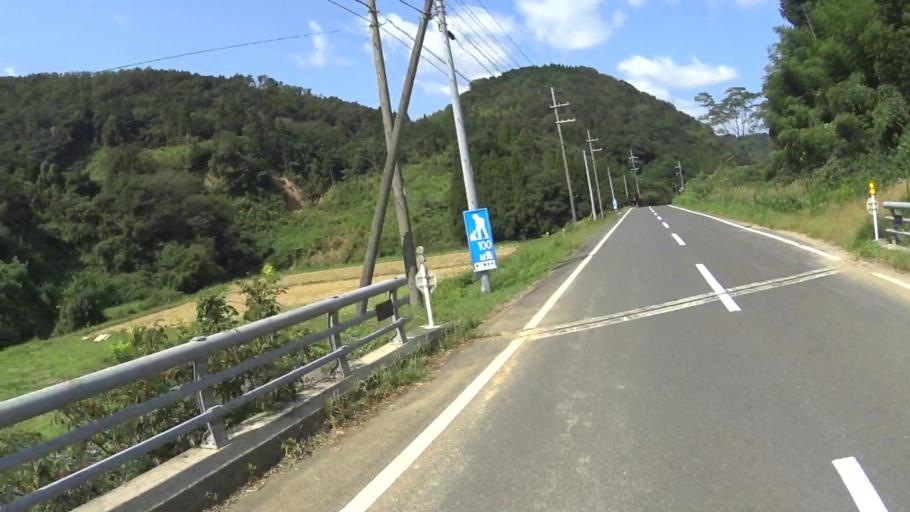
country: JP
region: Kyoto
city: Miyazu
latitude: 35.6917
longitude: 135.2514
